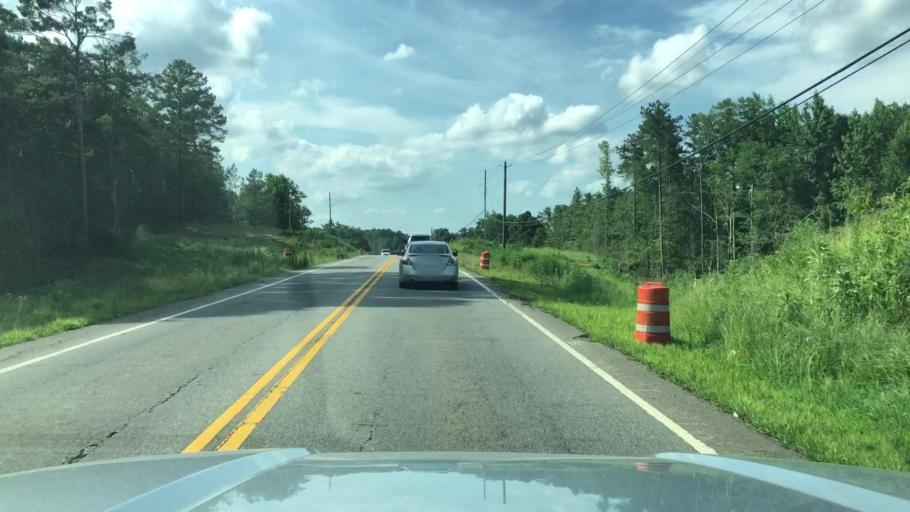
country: US
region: Georgia
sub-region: Douglas County
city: Douglasville
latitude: 33.7844
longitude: -84.7490
